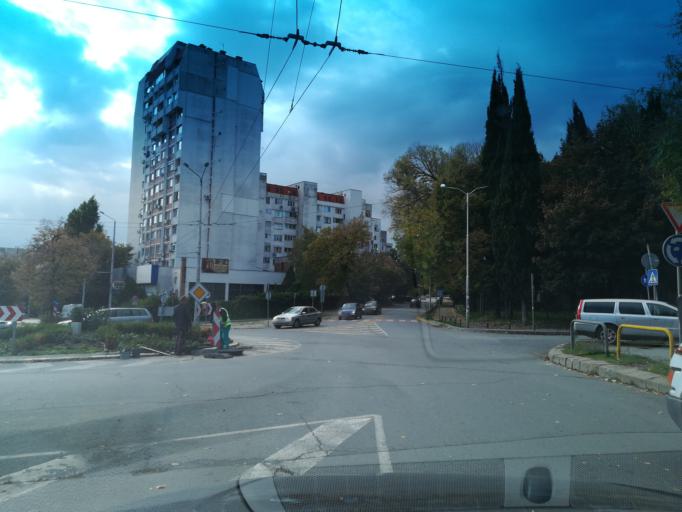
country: BG
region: Stara Zagora
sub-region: Obshtina Stara Zagora
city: Stara Zagora
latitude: 42.4370
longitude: 25.6311
